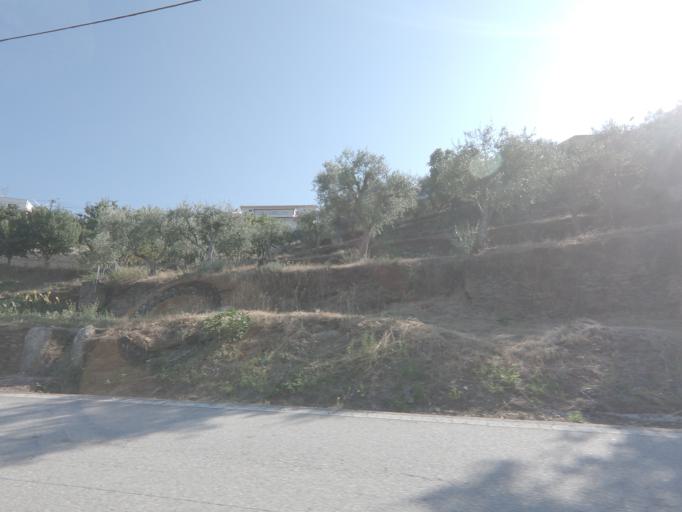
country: PT
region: Viseu
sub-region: Tabuaco
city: Tabuaco
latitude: 41.1161
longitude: -7.5618
